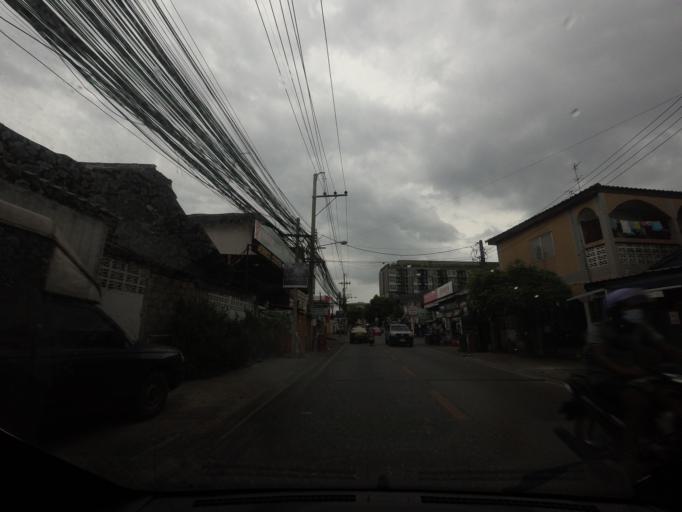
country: TH
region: Bangkok
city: Watthana
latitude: 13.7289
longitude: 100.6085
